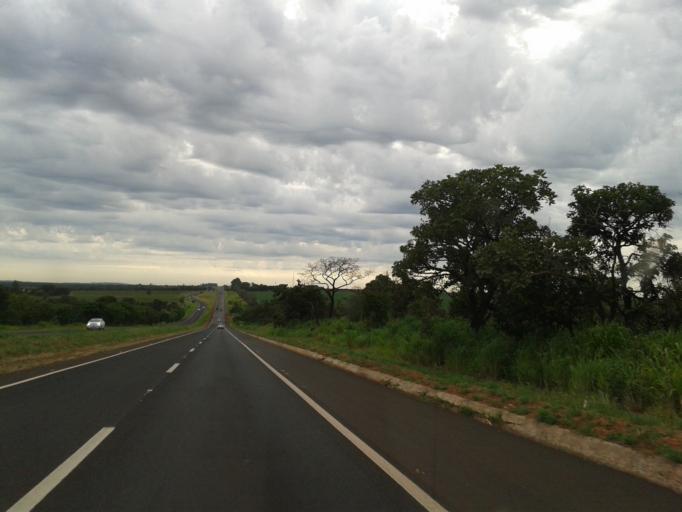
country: BR
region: Minas Gerais
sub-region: Monte Alegre De Minas
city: Monte Alegre de Minas
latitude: -18.8802
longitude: -49.0001
